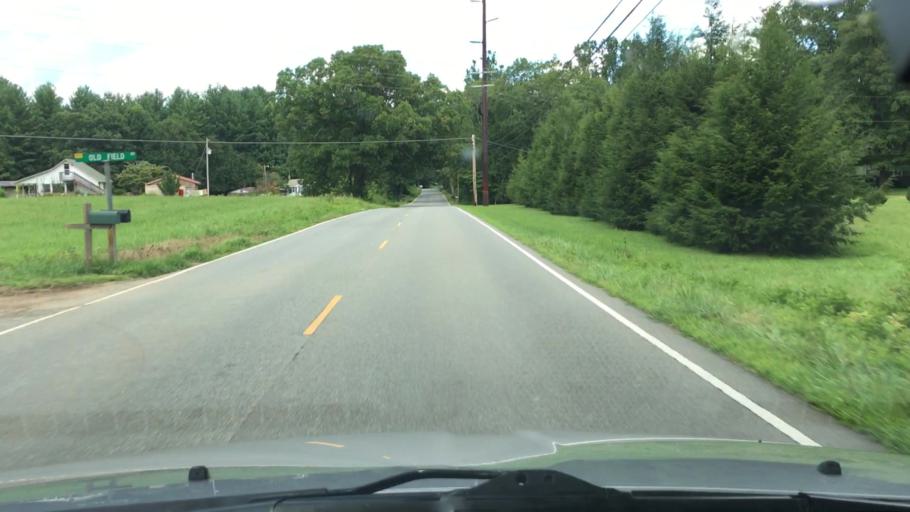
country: US
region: North Carolina
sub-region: Yancey County
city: Burnsville
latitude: 35.8200
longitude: -82.1913
